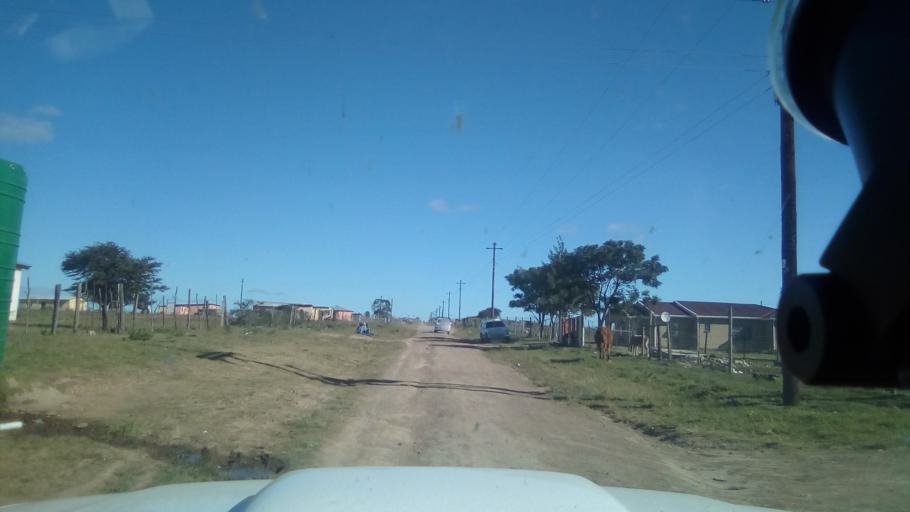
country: ZA
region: Eastern Cape
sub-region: Buffalo City Metropolitan Municipality
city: Bhisho
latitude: -32.7833
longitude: 27.3337
